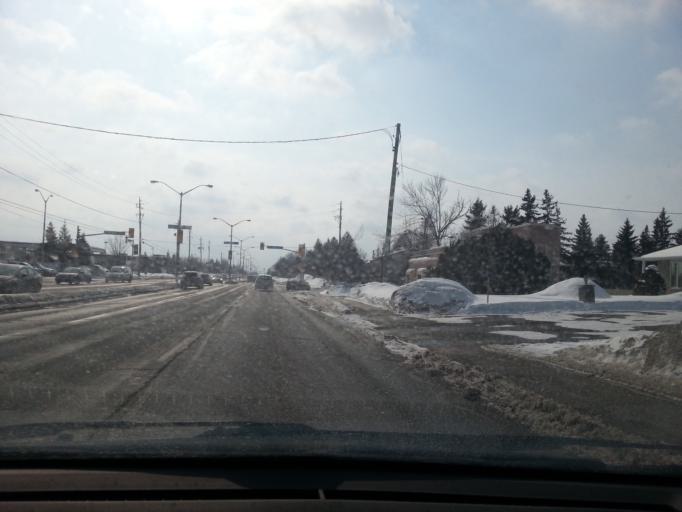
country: CA
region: Quebec
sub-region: Outaouais
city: Gatineau
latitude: 45.4684
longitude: -75.4922
